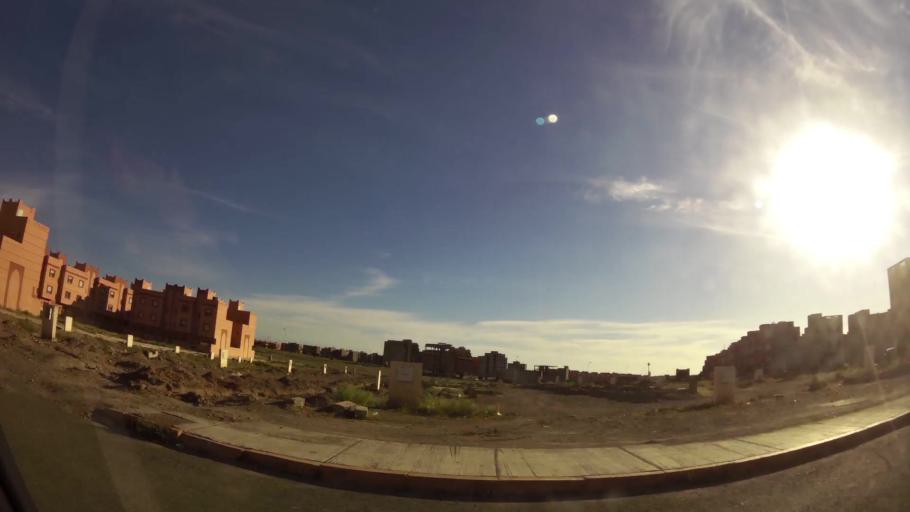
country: MA
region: Marrakech-Tensift-Al Haouz
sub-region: Marrakech
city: Marrakesh
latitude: 31.7572
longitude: -8.0992
